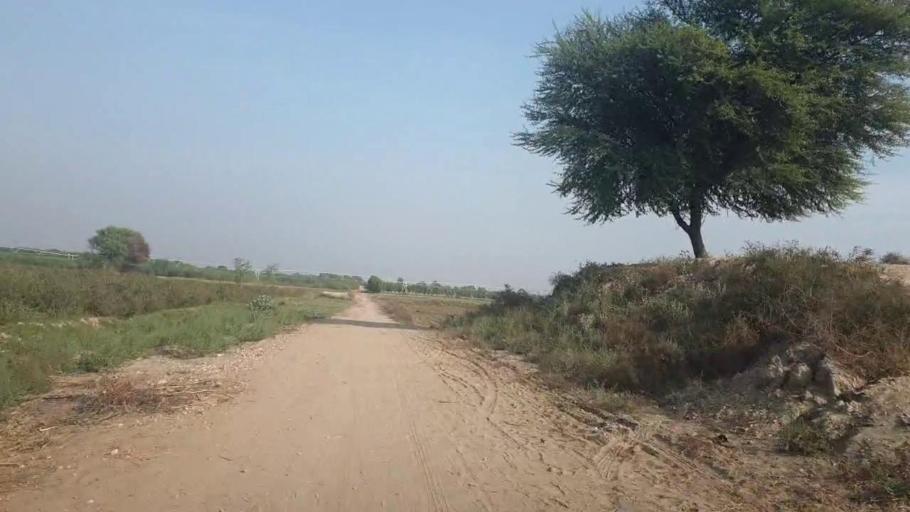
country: PK
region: Sindh
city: Tando Jam
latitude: 25.4295
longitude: 68.4720
